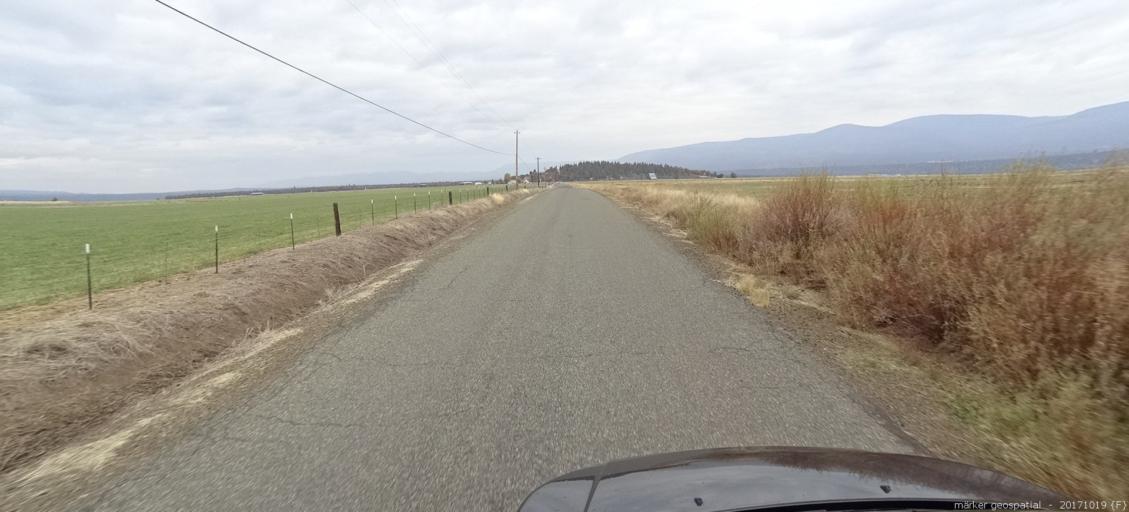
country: US
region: California
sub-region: Shasta County
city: Burney
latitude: 41.0813
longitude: -121.3652
